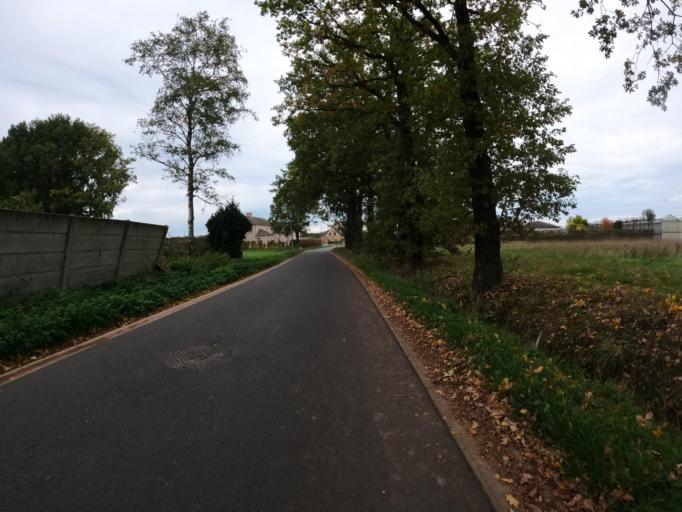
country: BE
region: Flanders
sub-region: Provincie Antwerpen
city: Hulshout
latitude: 51.0975
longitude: 4.8133
